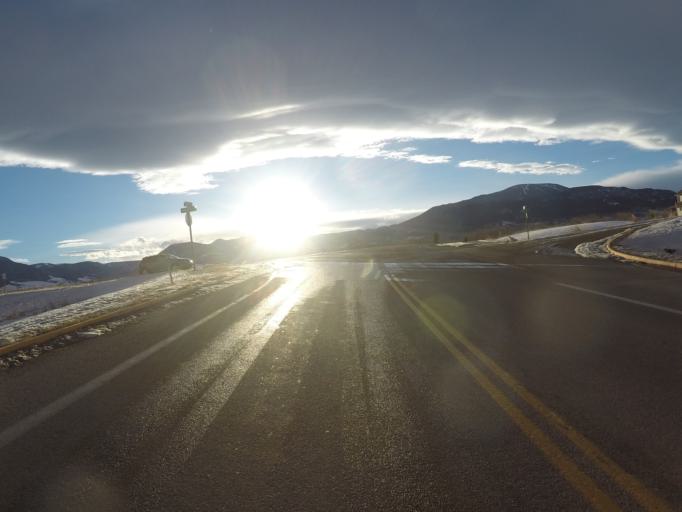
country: US
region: Montana
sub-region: Carbon County
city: Red Lodge
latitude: 45.1922
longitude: -109.2551
